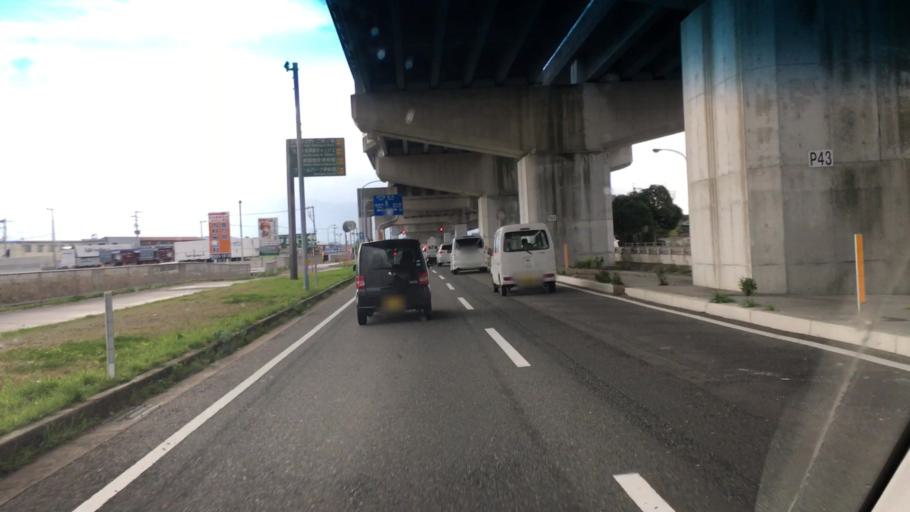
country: JP
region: Fukuoka
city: Maebaru-chuo
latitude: 33.5585
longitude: 130.2299
